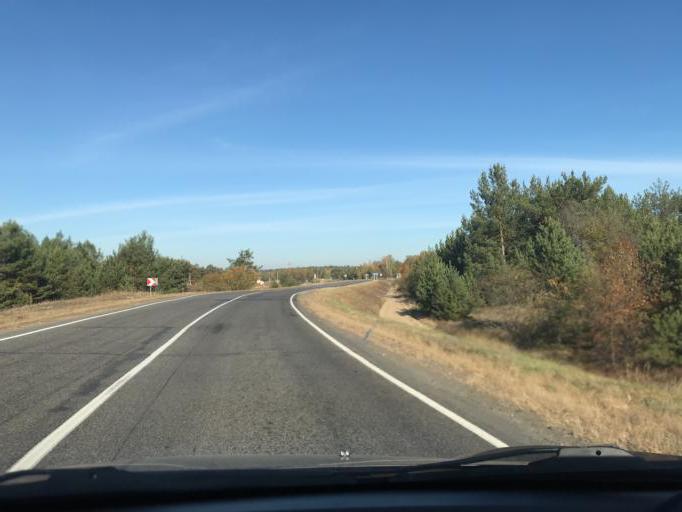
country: UA
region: Chernihiv
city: Lyubech
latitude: 51.5823
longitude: 30.4815
